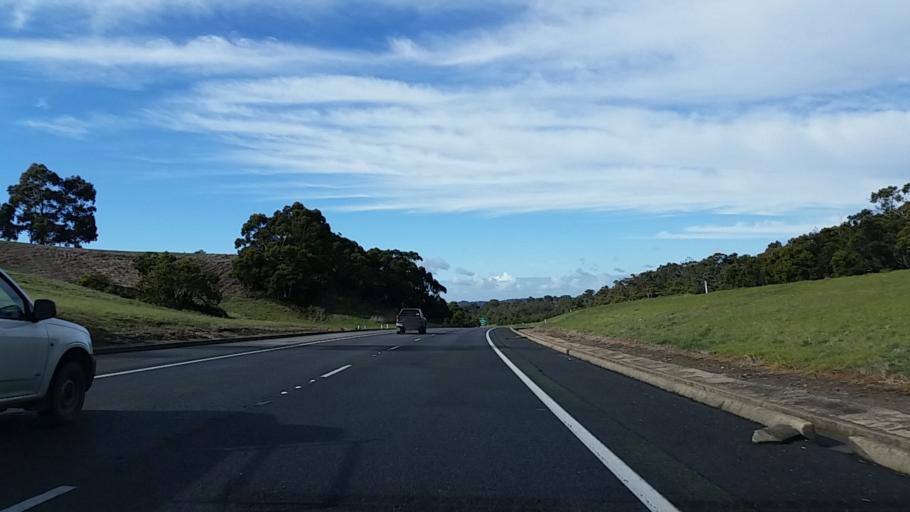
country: AU
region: South Australia
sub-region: Mount Barker
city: Little Hampton
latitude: -35.0523
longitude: 138.8322
